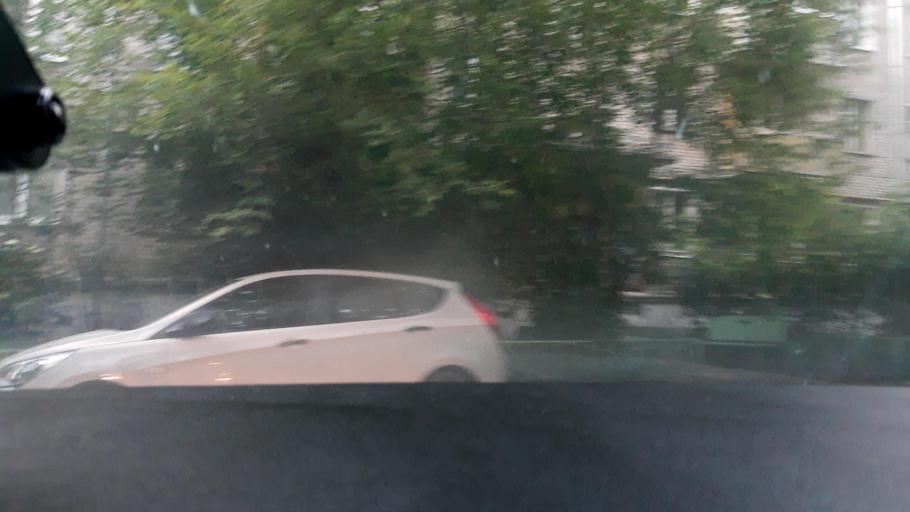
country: RU
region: Moskovskaya
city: Pavshino
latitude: 55.8225
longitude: 37.3409
